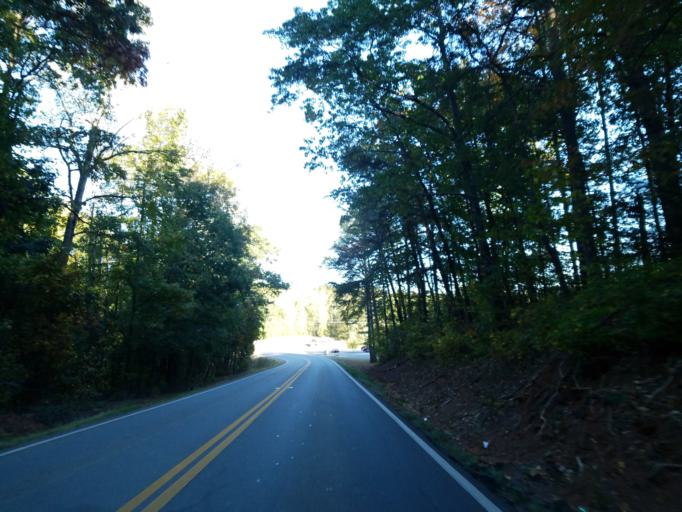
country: US
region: Georgia
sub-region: Dawson County
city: Dawsonville
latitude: 34.4241
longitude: -84.2367
